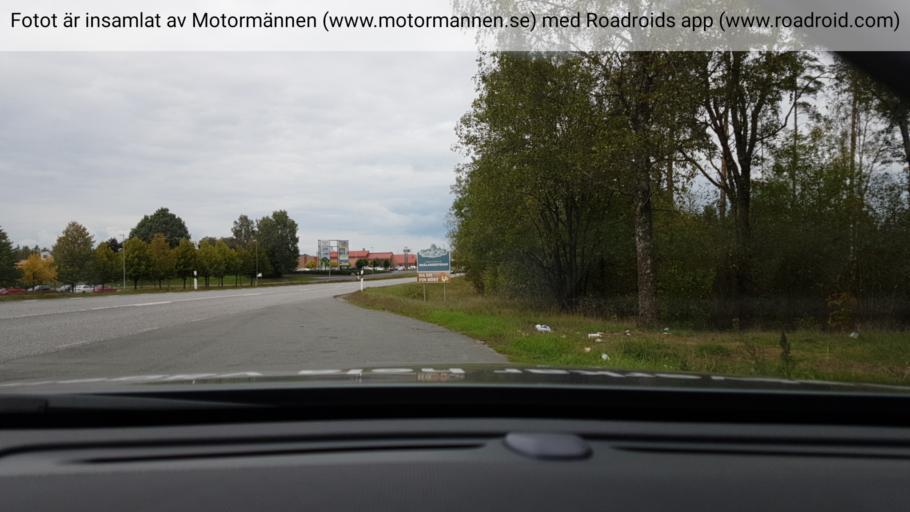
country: SE
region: Joenkoeping
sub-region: Gislaveds Kommun
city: Smalandsstenar
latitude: 57.1421
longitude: 13.3845
